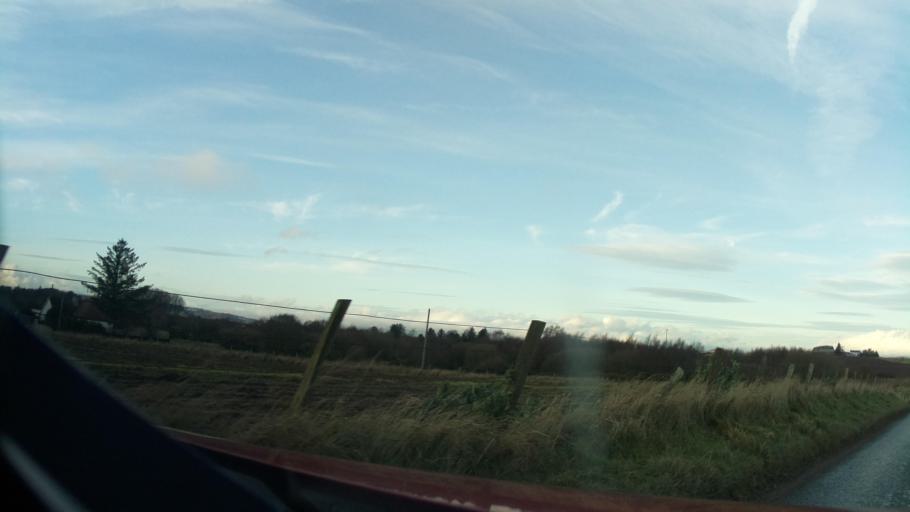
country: GB
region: Scotland
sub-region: Angus
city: Letham
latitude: 56.5754
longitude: -2.7800
